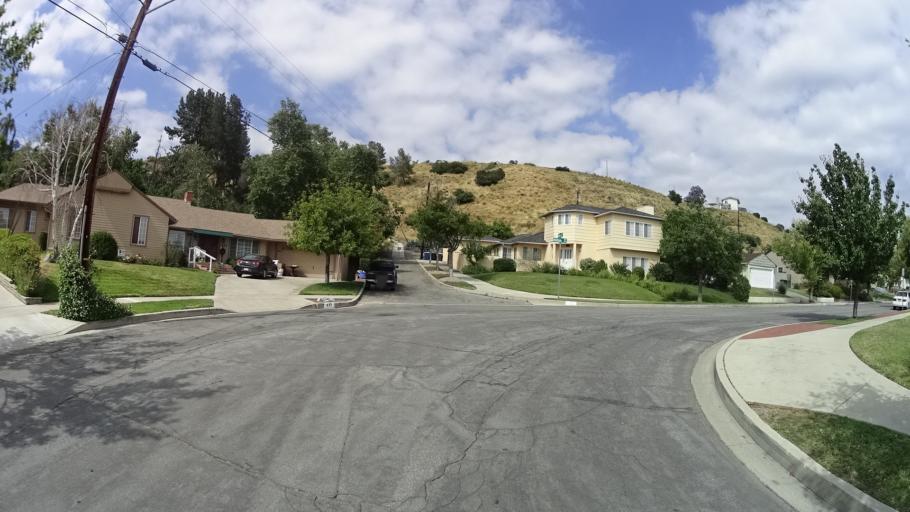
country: US
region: California
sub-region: Los Angeles County
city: Burbank
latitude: 34.2021
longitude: -118.3187
